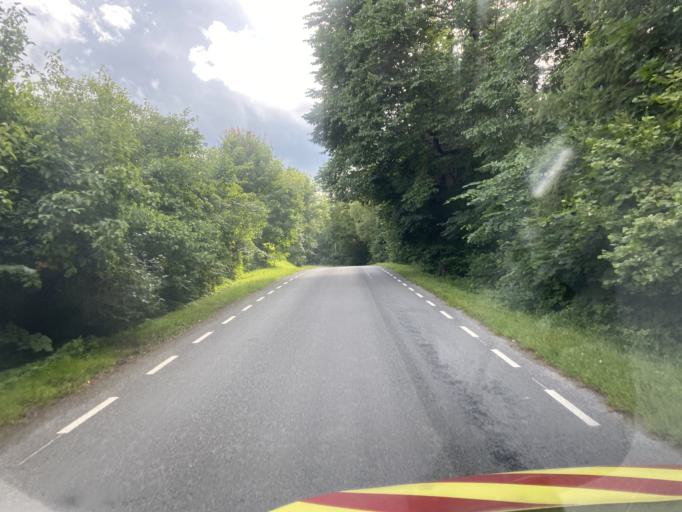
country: EE
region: Viljandimaa
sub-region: Viljandi linn
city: Viljandi
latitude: 58.3927
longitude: 25.6008
